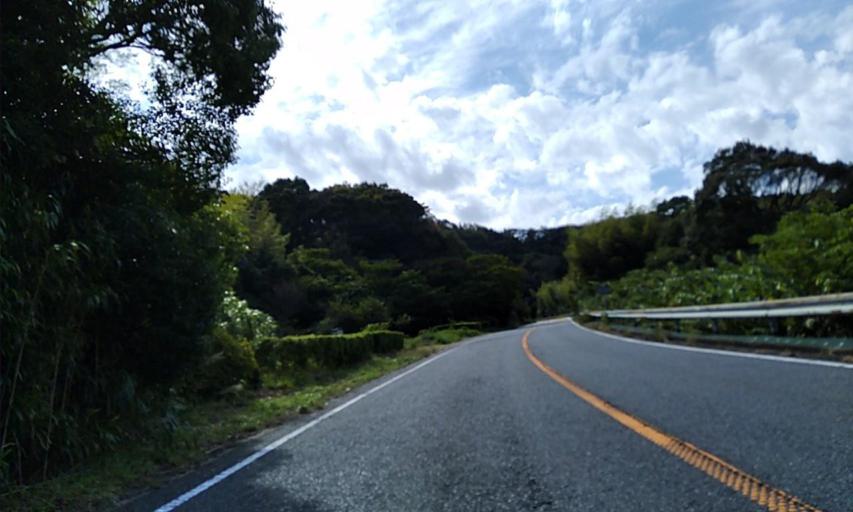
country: JP
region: Wakayama
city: Gobo
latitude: 33.9590
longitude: 135.1239
